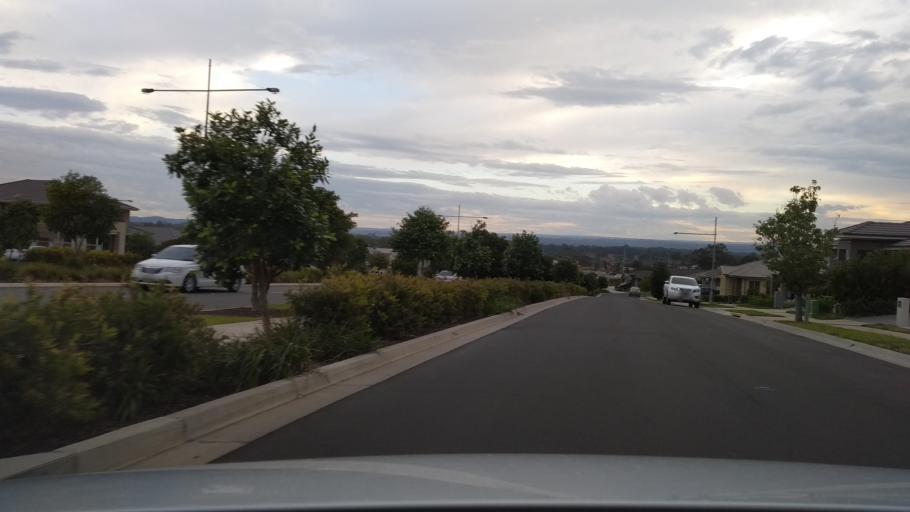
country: AU
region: New South Wales
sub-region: Camden
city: Narellan
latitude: -34.0049
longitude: 150.7283
